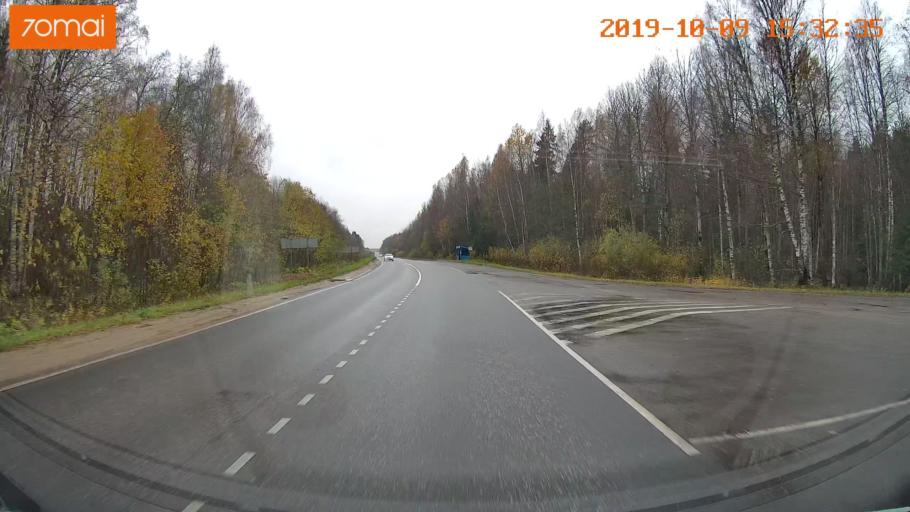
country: RU
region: Kostroma
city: Oktyabr'skiy
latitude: 57.9633
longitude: 41.2739
